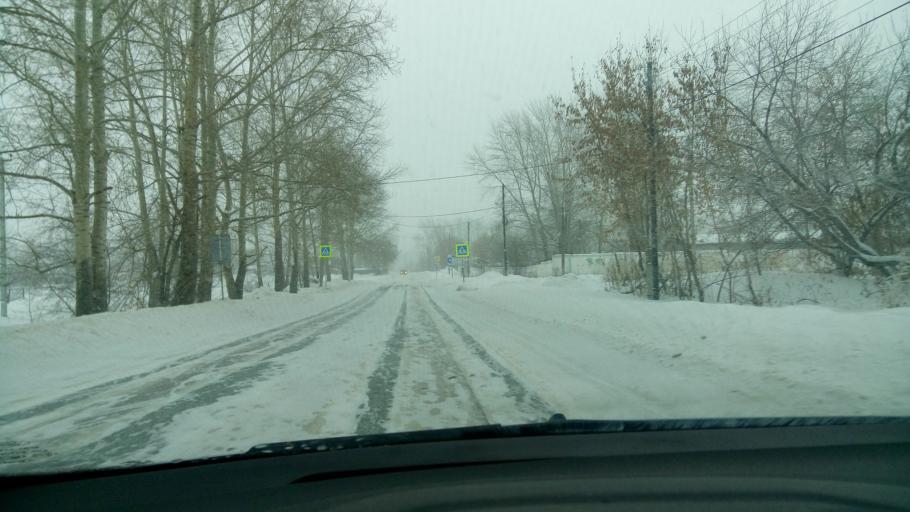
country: RU
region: Sverdlovsk
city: Bogdanovich
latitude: 56.7819
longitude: 62.0469
